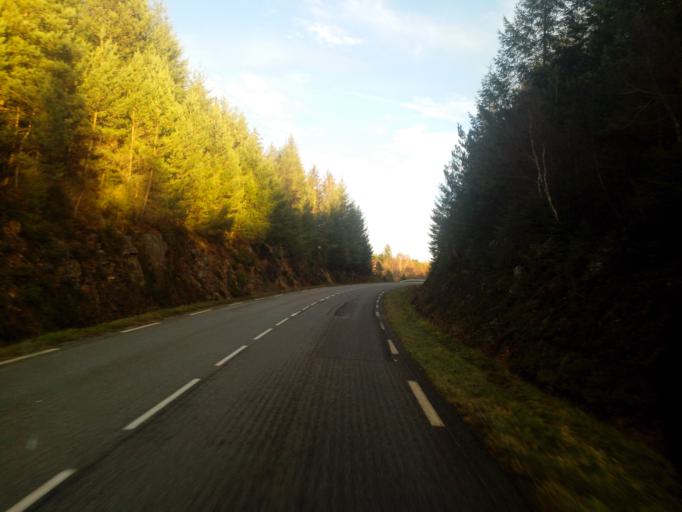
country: FR
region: Limousin
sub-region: Departement de la Correze
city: Meymac
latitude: 45.5765
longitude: 2.0957
